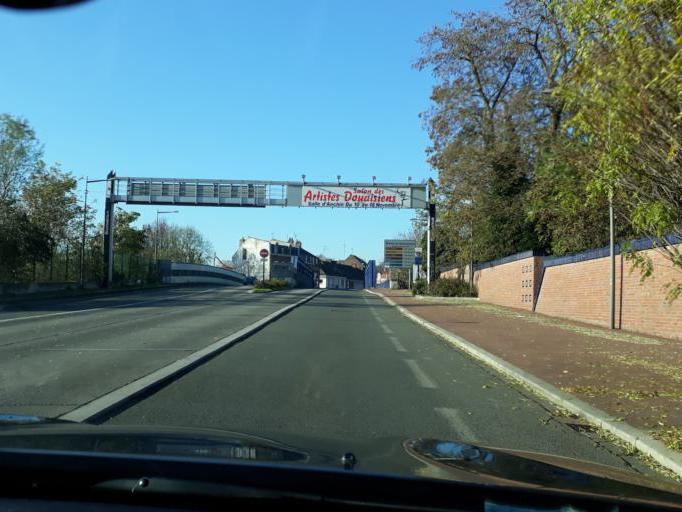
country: FR
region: Nord-Pas-de-Calais
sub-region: Departement du Nord
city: Dechy
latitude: 50.3644
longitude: 3.0937
